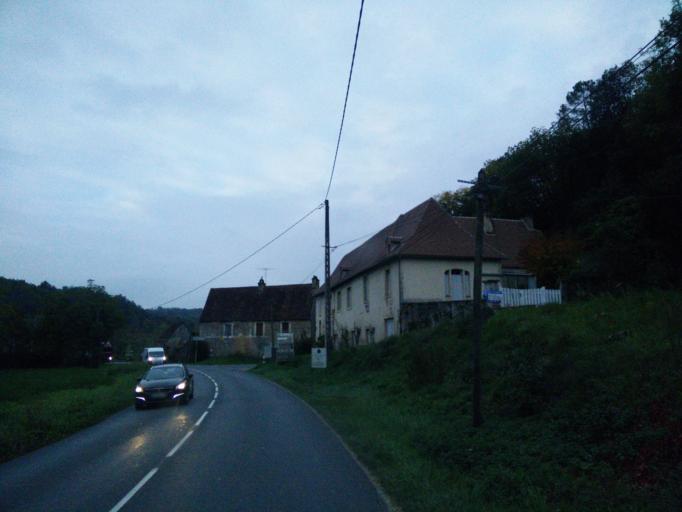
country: FR
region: Aquitaine
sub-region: Departement de la Dordogne
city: Carsac-Aillac
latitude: 44.8464
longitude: 1.2723
